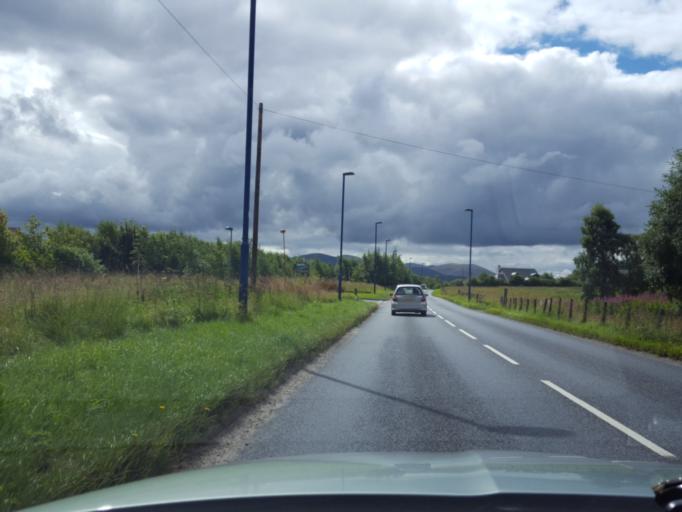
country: GB
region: Scotland
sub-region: Highland
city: Aviemore
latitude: 57.2054
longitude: -3.8267
